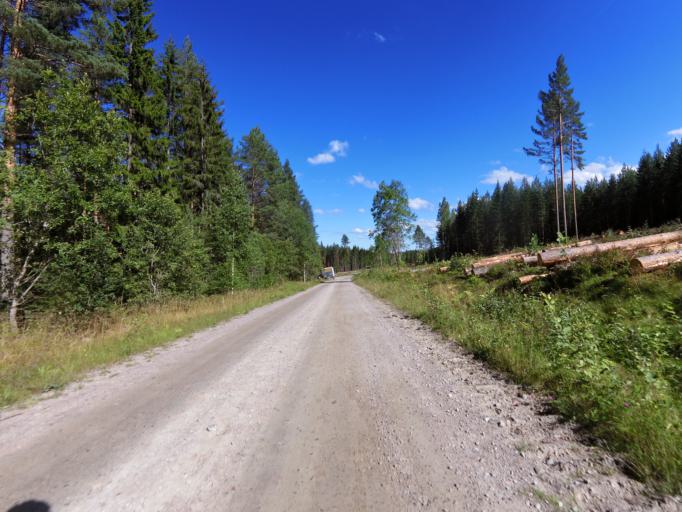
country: SE
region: Gaevleborg
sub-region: Hofors Kommun
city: Hofors
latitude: 60.5082
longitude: 16.3947
